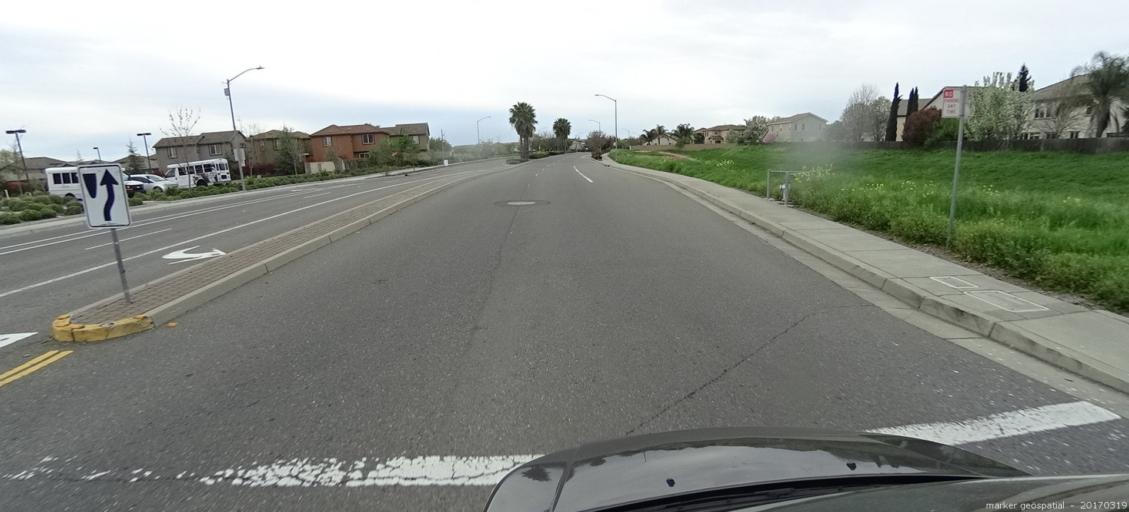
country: US
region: California
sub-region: Sacramento County
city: Elverta
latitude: 38.6801
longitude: -121.5315
